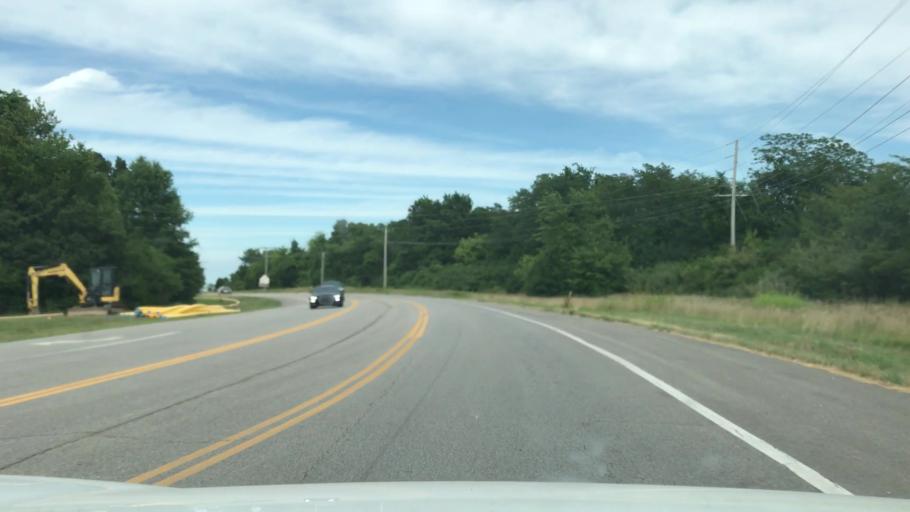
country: US
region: Missouri
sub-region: Saint Charles County
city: Weldon Spring
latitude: 38.7012
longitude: -90.7138
